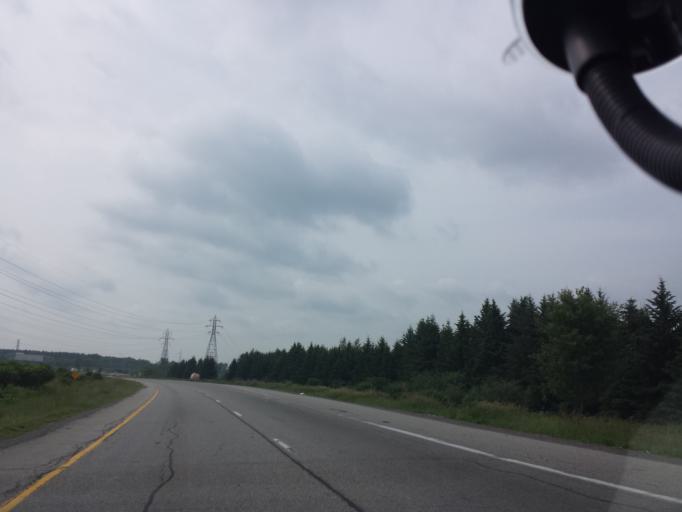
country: CA
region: Ontario
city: Ottawa
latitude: 45.4062
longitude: -75.5978
